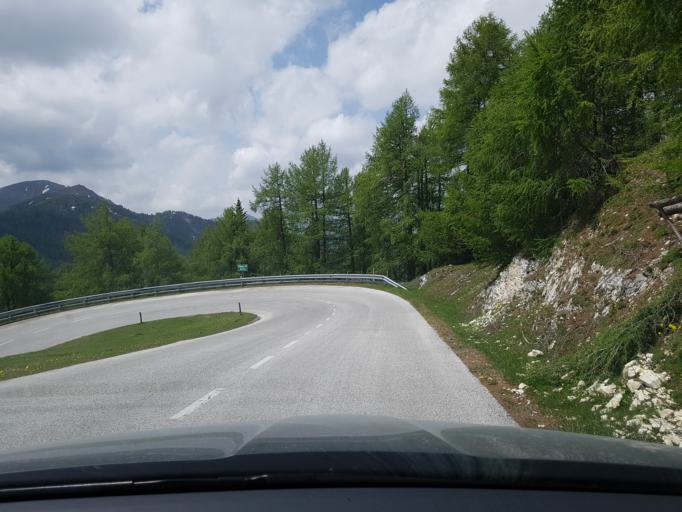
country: AT
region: Carinthia
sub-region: Politischer Bezirk Spittal an der Drau
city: Kleinkirchheim
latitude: 46.9255
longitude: 13.7561
